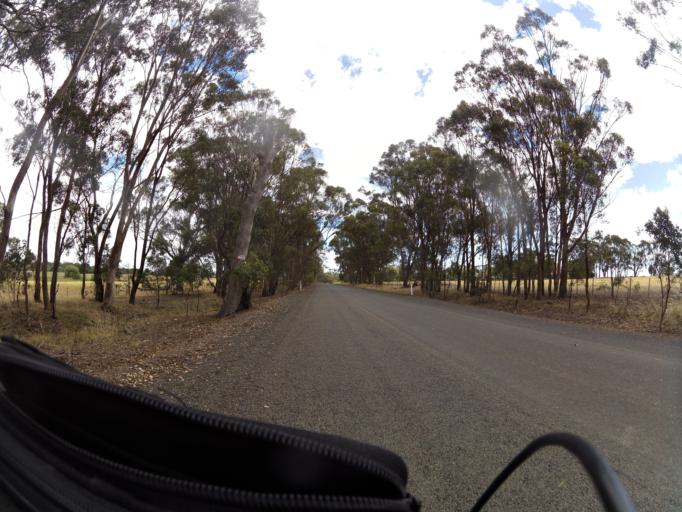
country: AU
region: Victoria
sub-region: Campaspe
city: Kyabram
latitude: -36.7375
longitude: 145.1407
